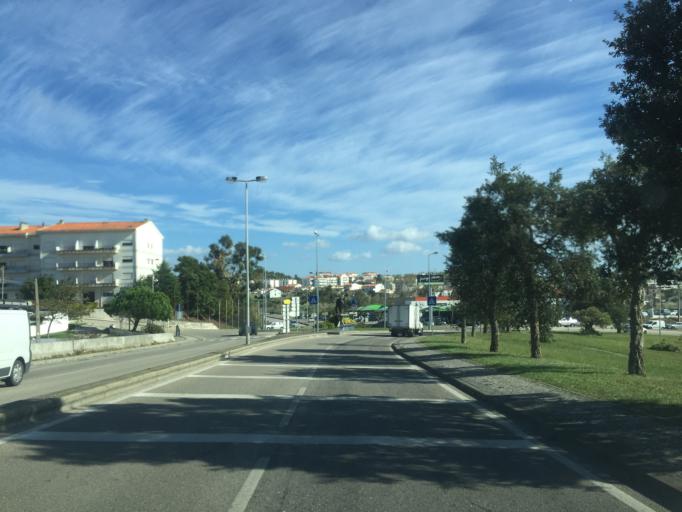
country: PT
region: Coimbra
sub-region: Figueira da Foz
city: Tavarede
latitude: 40.1639
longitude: -8.8491
